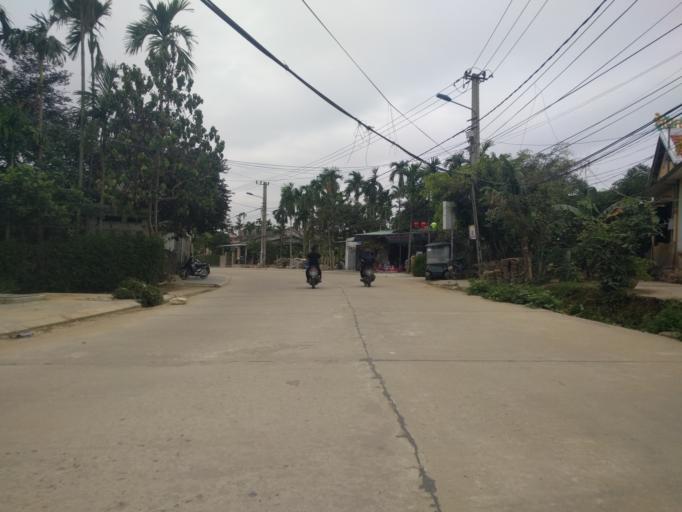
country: VN
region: Quang Nam
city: Hoi An
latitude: 15.8709
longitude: 108.3470
